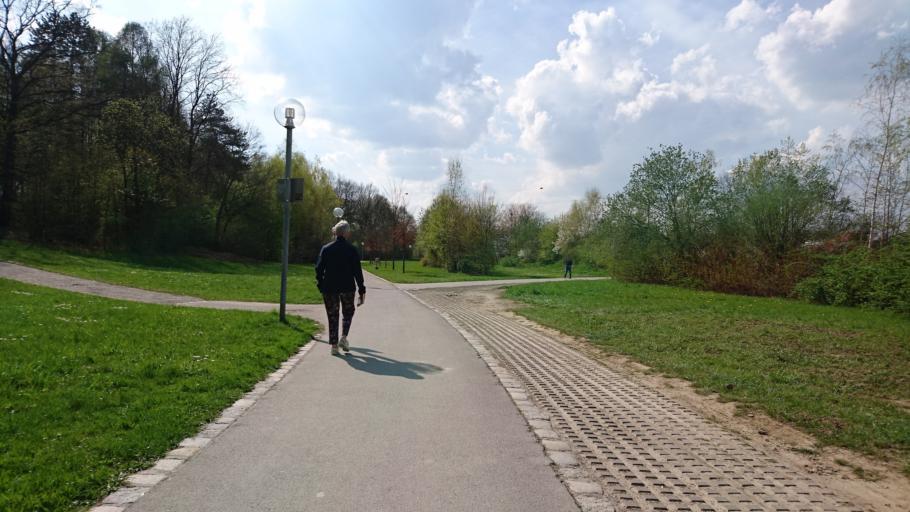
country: DE
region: Bavaria
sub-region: Swabia
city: Stadtbergen
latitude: 48.3839
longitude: 10.8357
